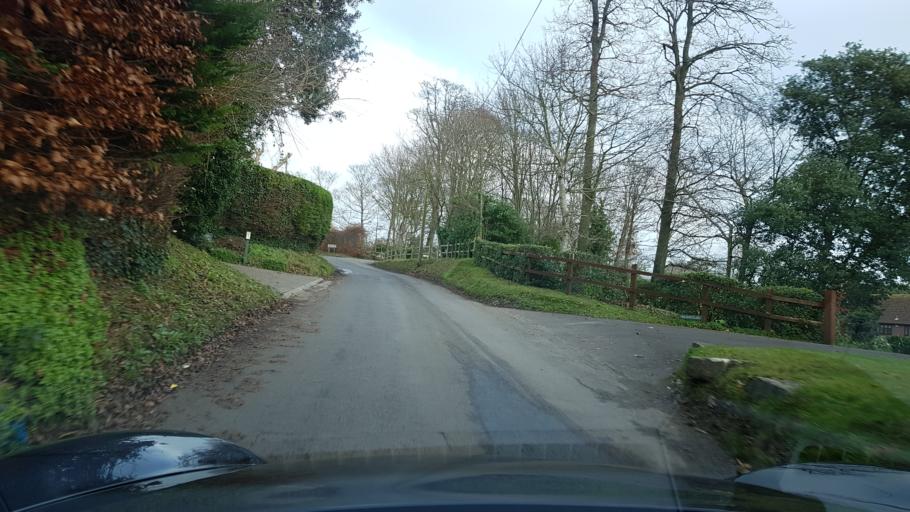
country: GB
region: England
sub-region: Dorset
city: Bridport
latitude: 50.7074
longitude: -2.7232
